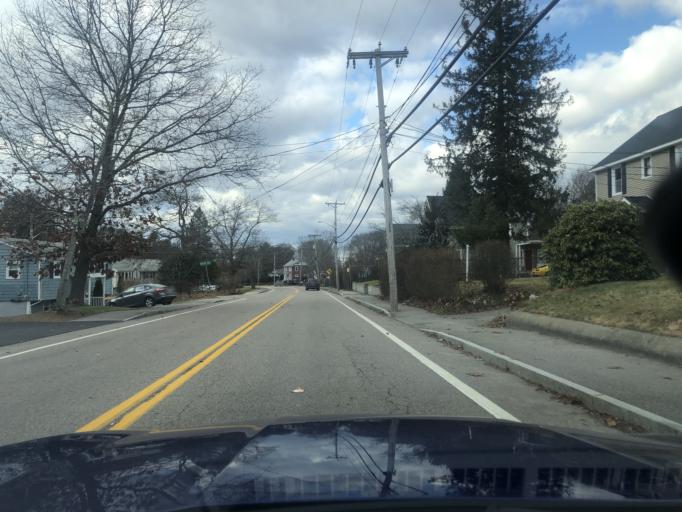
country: US
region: Massachusetts
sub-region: Plymouth County
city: Brockton
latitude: 42.1070
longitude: -71.0053
